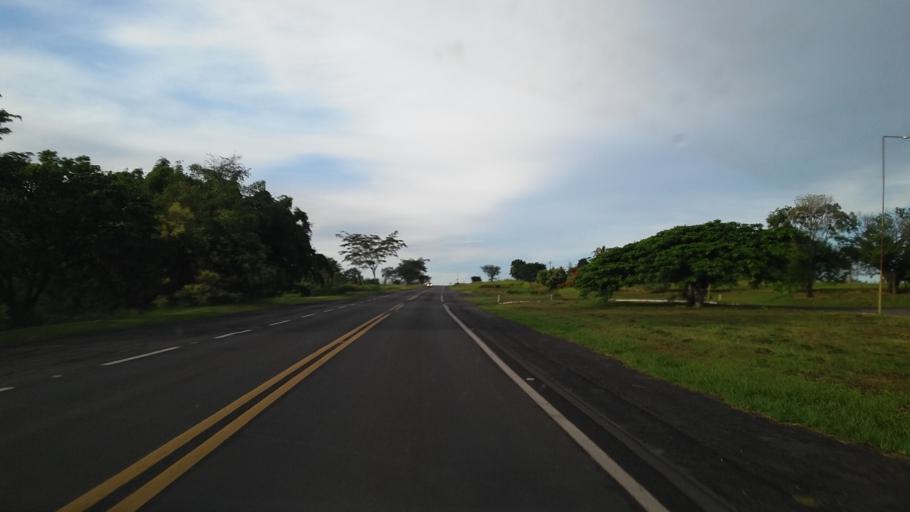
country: BR
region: Sao Paulo
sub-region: Marilia
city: Marilia
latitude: -21.9201
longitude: -49.9165
